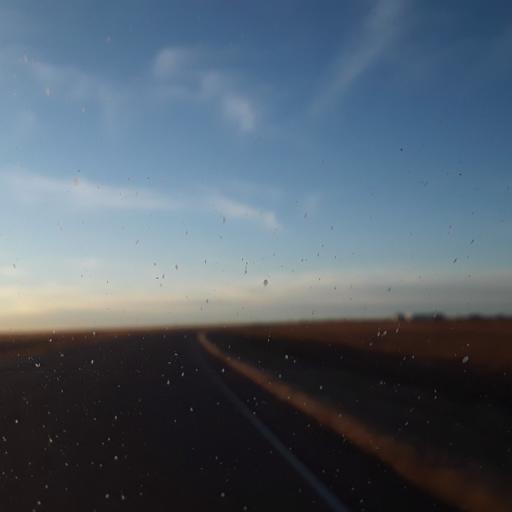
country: US
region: Colorado
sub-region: Cheyenne County
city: Cheyenne Wells
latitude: 38.8091
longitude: -102.4518
